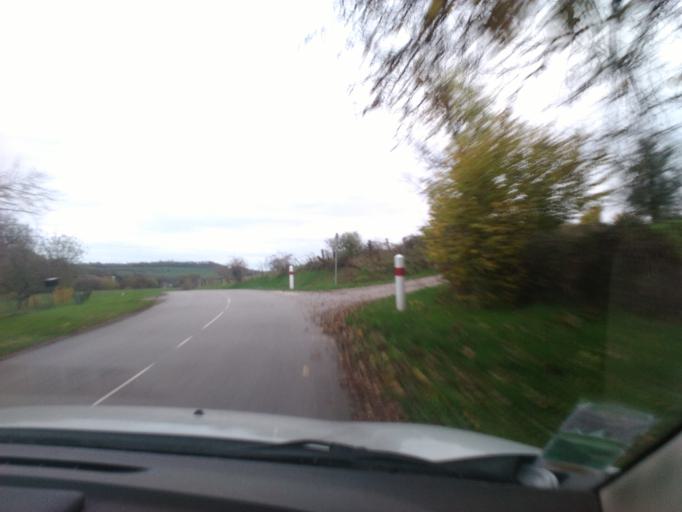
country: FR
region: Lorraine
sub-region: Departement des Vosges
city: Vincey
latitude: 48.2633
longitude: 6.2723
